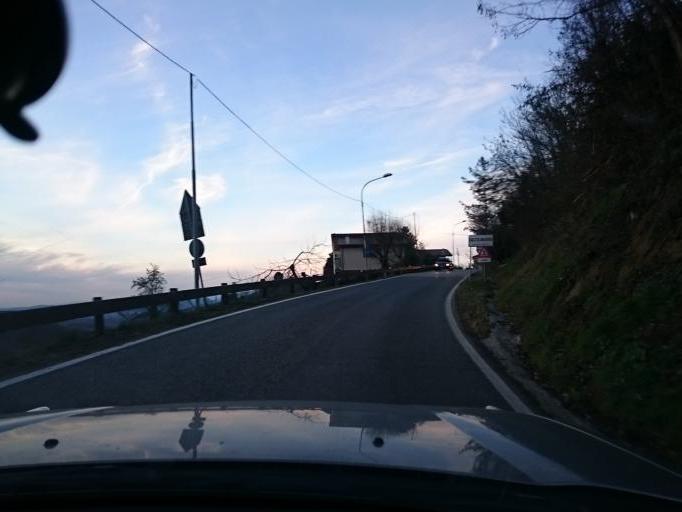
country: IT
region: Veneto
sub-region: Provincia di Padova
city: Vo
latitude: 45.3293
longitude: 11.6849
